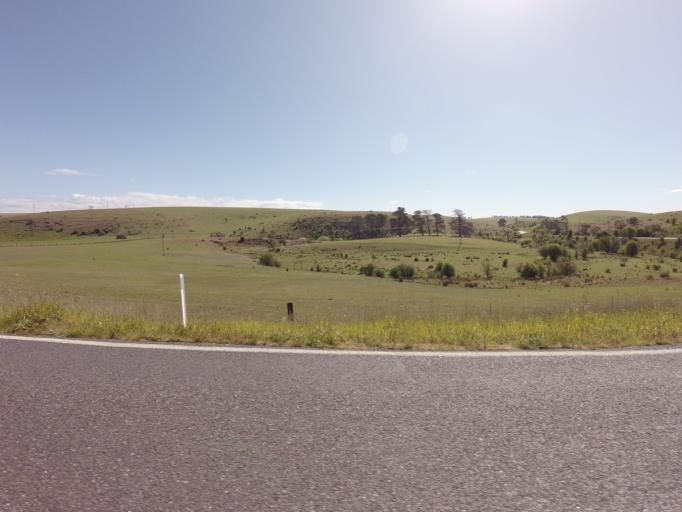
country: AU
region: Tasmania
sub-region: Derwent Valley
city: New Norfolk
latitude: -42.6541
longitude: 146.9357
